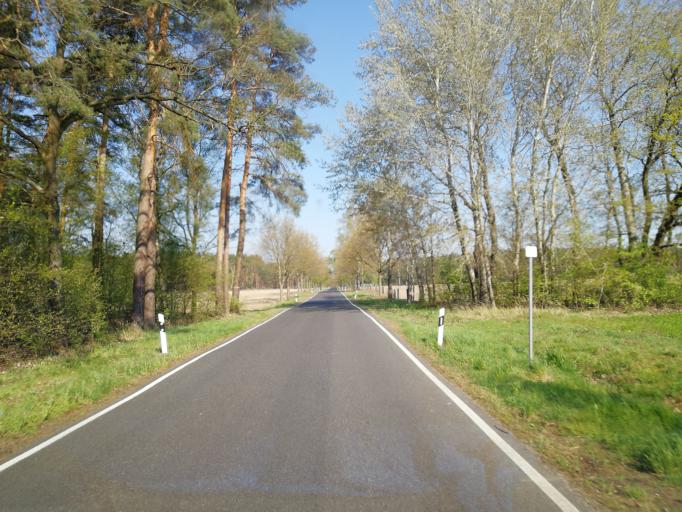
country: DE
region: Brandenburg
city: Bronkow
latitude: 51.7104
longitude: 13.8700
